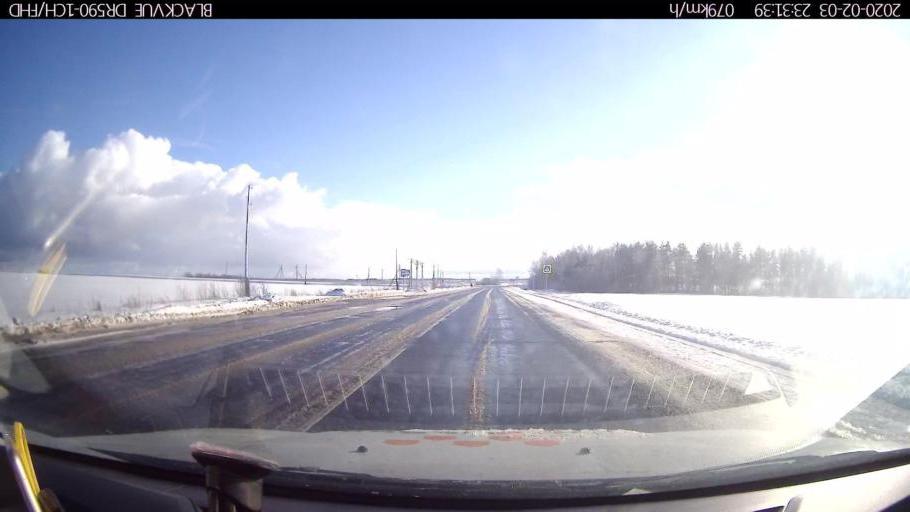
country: RU
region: Nizjnij Novgorod
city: Dal'neye Konstantinovo
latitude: 55.9397
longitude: 44.2278
